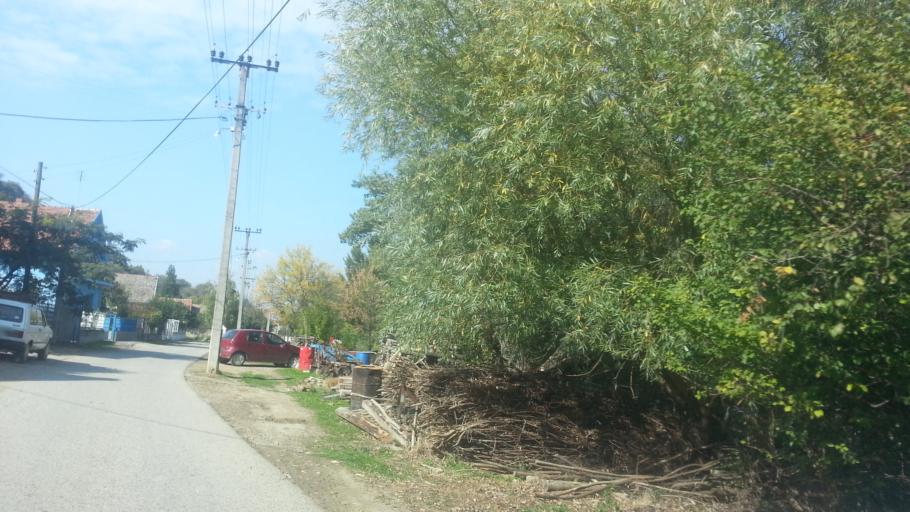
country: RS
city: Novi Slankamen
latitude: 45.1483
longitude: 20.2504
